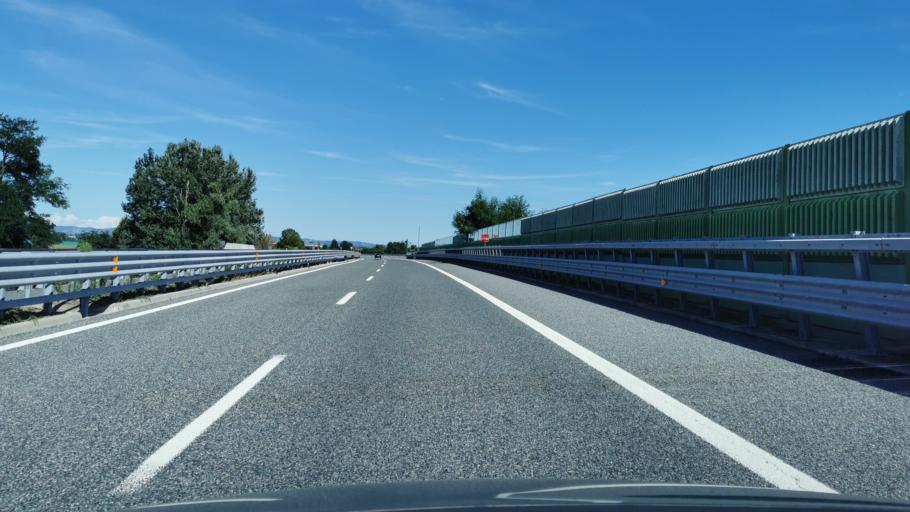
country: IT
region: Piedmont
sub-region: Provincia di Cuneo
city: Sant'Albano Stura
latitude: 44.4698
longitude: 7.7142
